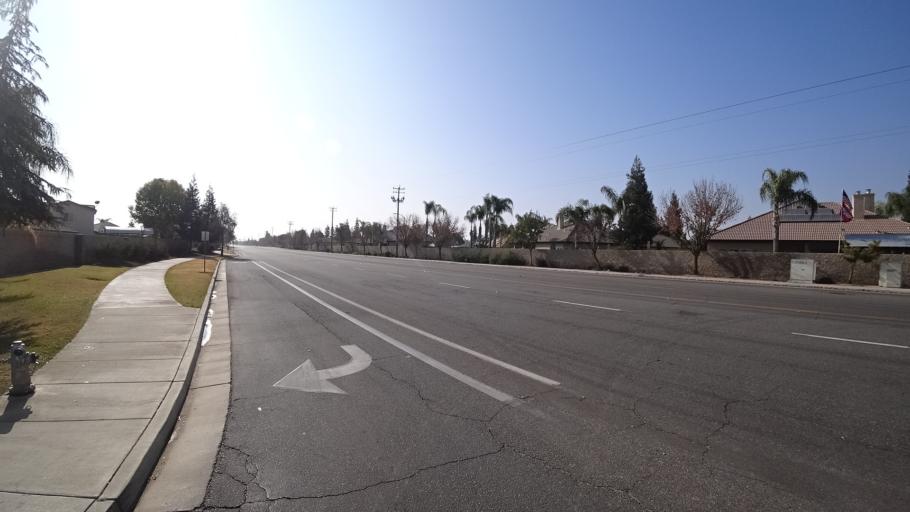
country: US
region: California
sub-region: Kern County
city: Rosedale
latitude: 35.4166
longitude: -119.1276
